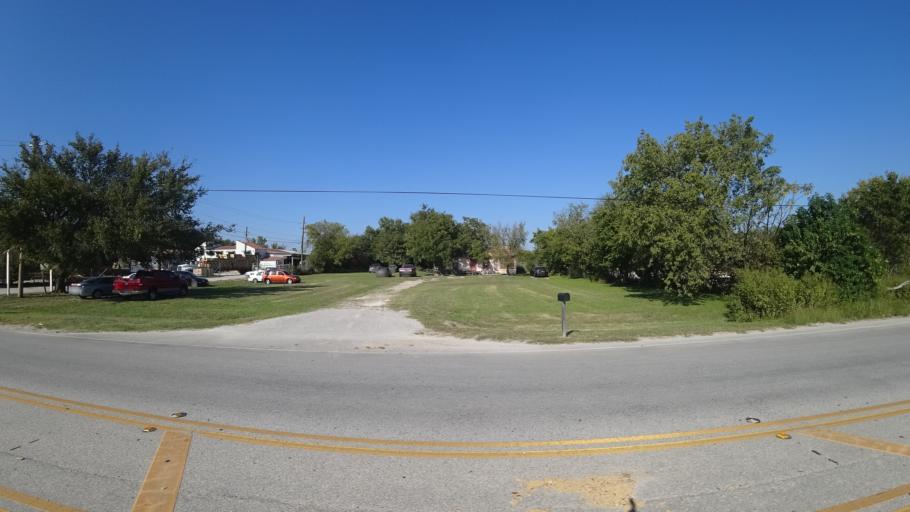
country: US
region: Texas
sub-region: Travis County
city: Wells Branch
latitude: 30.3423
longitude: -97.6640
